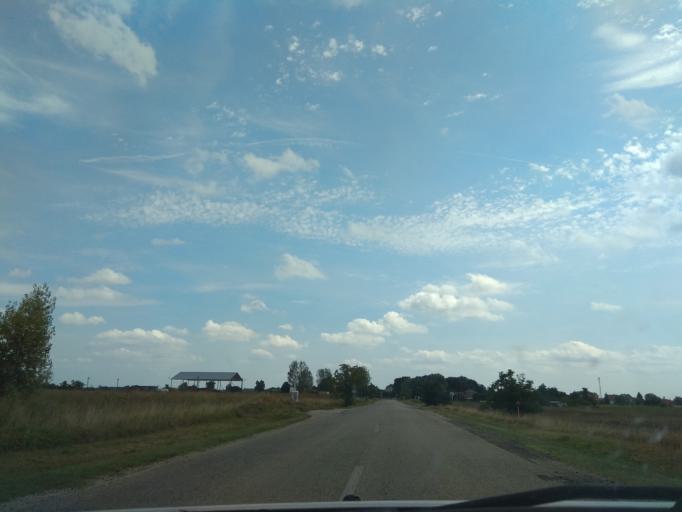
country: HU
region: Borsod-Abauj-Zemplen
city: Sajolad
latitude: 48.0434
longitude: 20.8791
